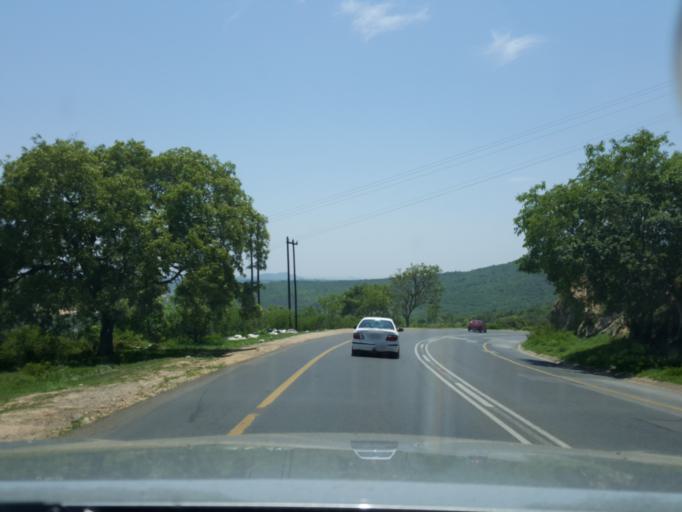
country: ZA
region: Limpopo
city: Thulamahashi
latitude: -24.8317
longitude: 31.0756
